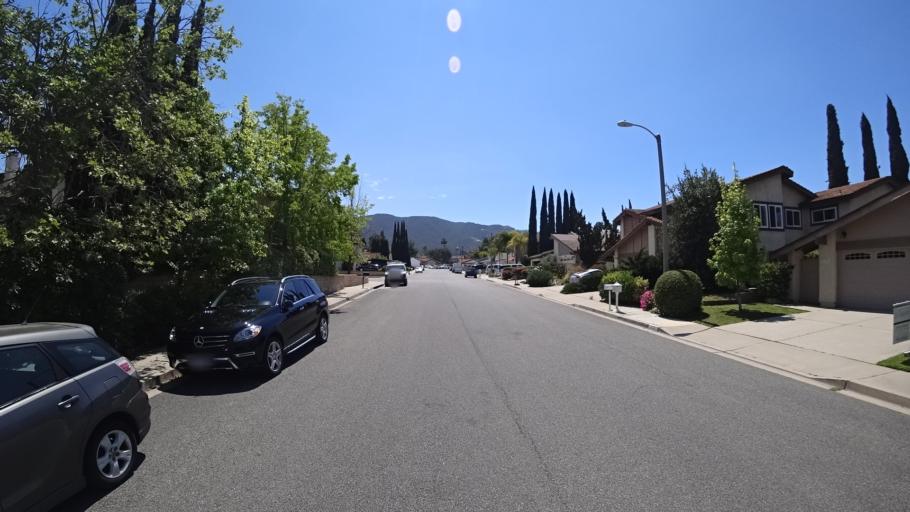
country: US
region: California
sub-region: Ventura County
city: Casa Conejo
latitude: 34.1815
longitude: -118.9202
